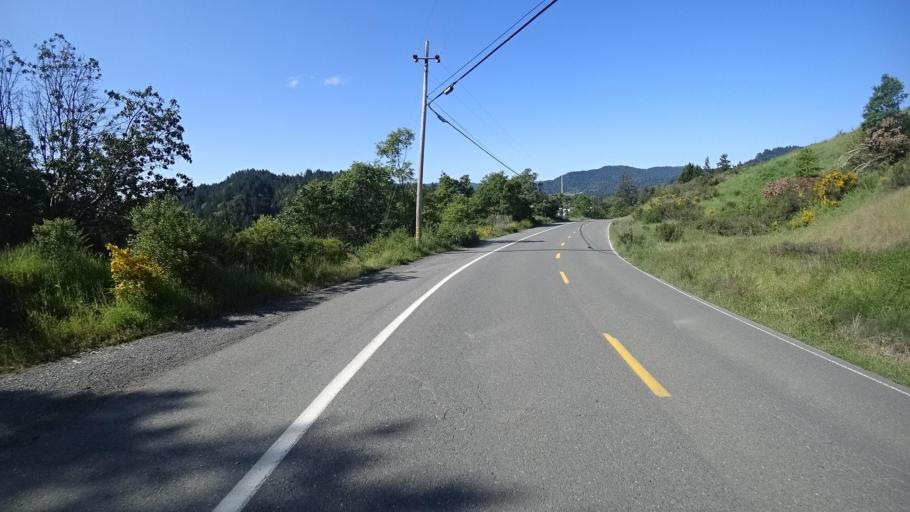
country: US
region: California
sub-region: Humboldt County
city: Redway
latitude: 40.1058
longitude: -123.7858
